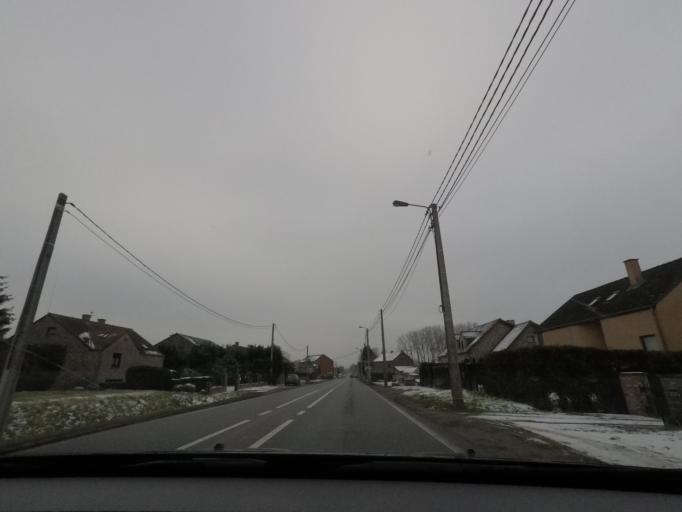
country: BE
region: Wallonia
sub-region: Province de Namur
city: Fosses-la-Ville
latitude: 50.4753
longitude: 4.6724
